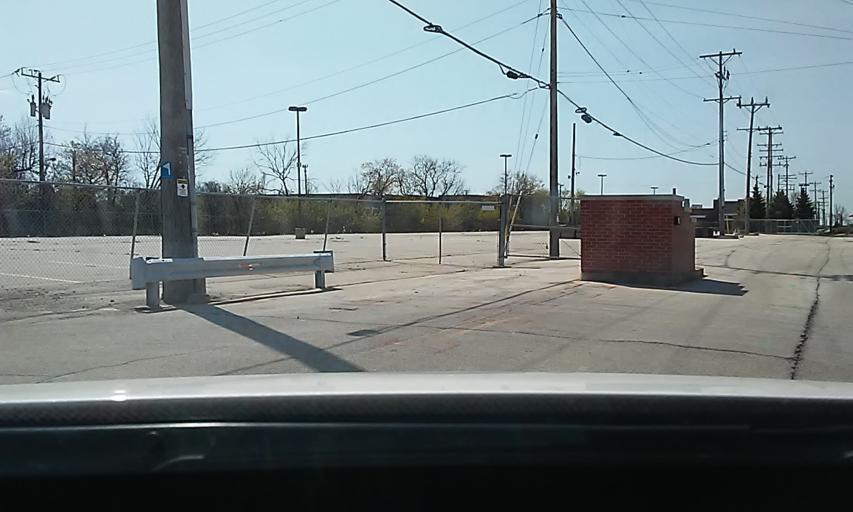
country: US
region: Wisconsin
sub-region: Milwaukee County
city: West Milwaukee
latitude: 43.0206
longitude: -87.9677
